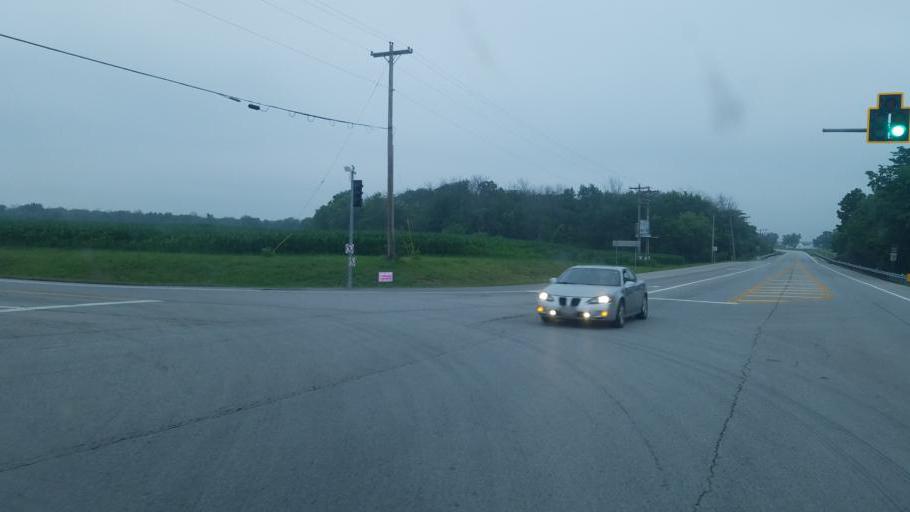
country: US
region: Ohio
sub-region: Fayette County
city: Washington Court House
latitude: 39.5639
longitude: -83.4072
